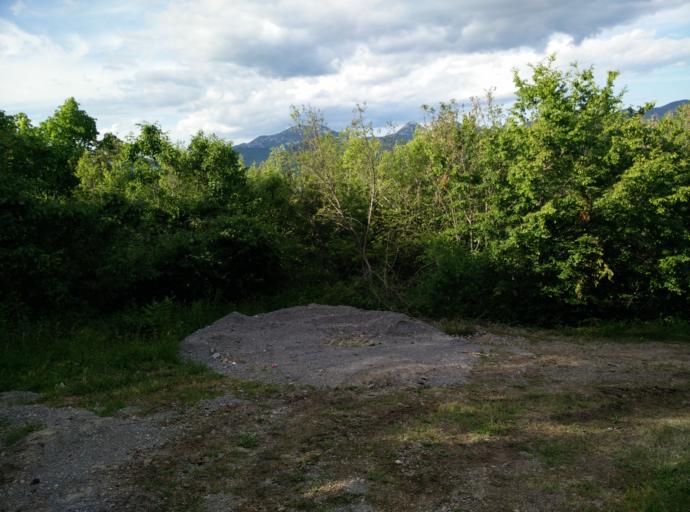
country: HR
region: Zadarska
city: Obrovac
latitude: 44.3845
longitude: 15.6739
